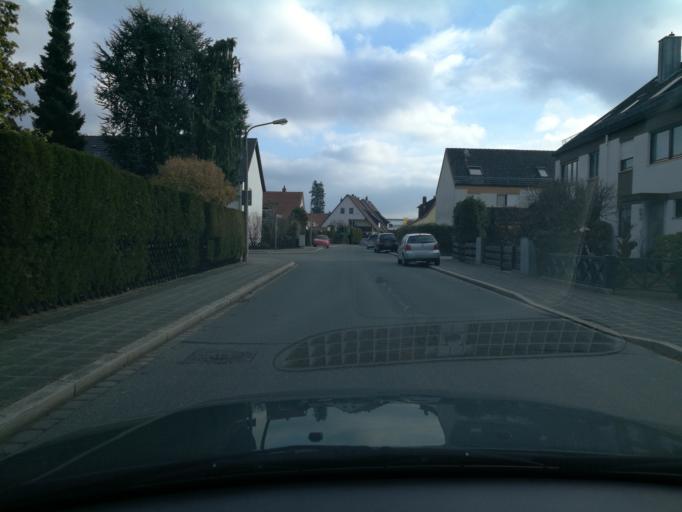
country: DE
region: Bavaria
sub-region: Regierungsbezirk Mittelfranken
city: Grossreuth bei Schweinau
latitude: 49.4542
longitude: 11.0248
